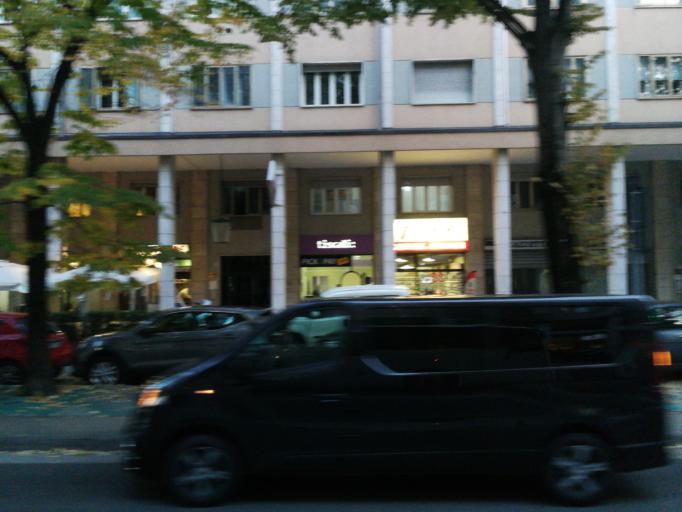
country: IT
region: Veneto
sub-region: Provincia di Venezia
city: Mestre
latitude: 45.4899
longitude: 12.2445
